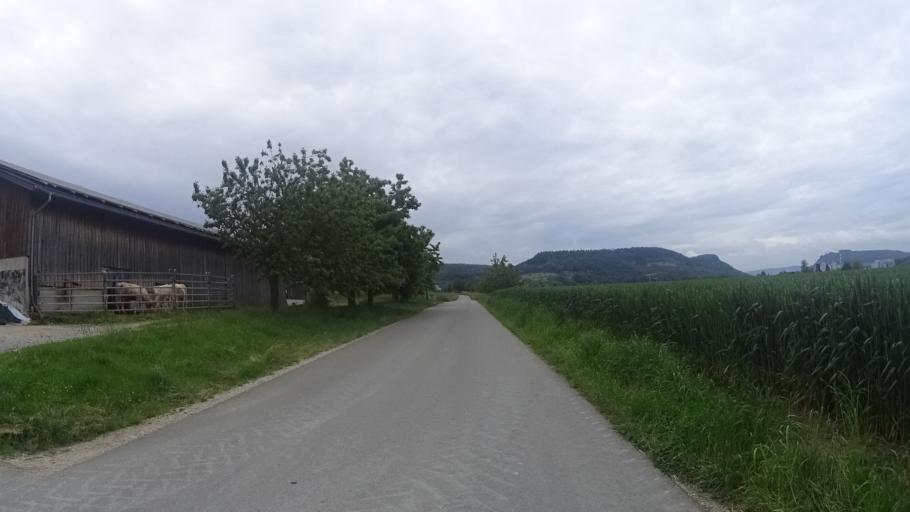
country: CH
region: Aargau
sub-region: Bezirk Baden
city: Wurenlingen
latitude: 47.5433
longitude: 8.2551
